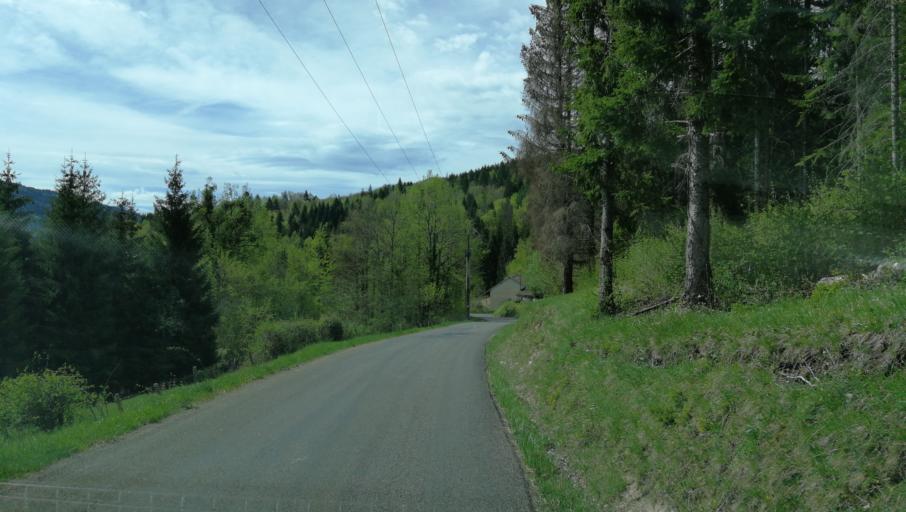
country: FR
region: Rhone-Alpes
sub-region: Departement de l'Ain
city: Oyonnax
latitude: 46.2254
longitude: 5.7448
